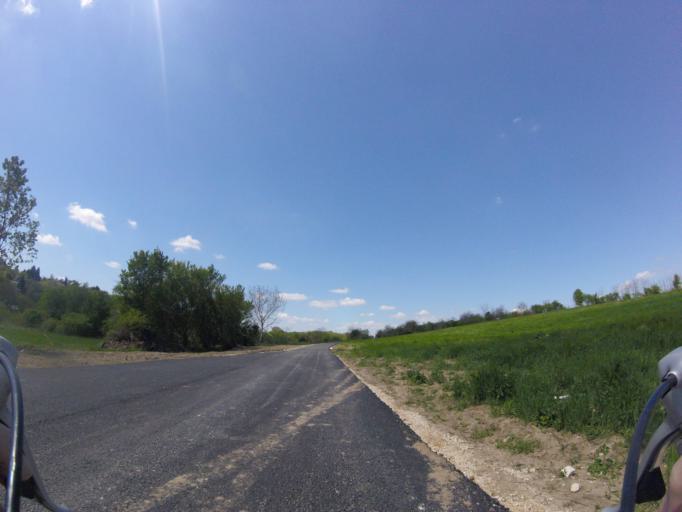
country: HU
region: Pest
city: Budaors
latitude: 47.4405
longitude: 18.9592
